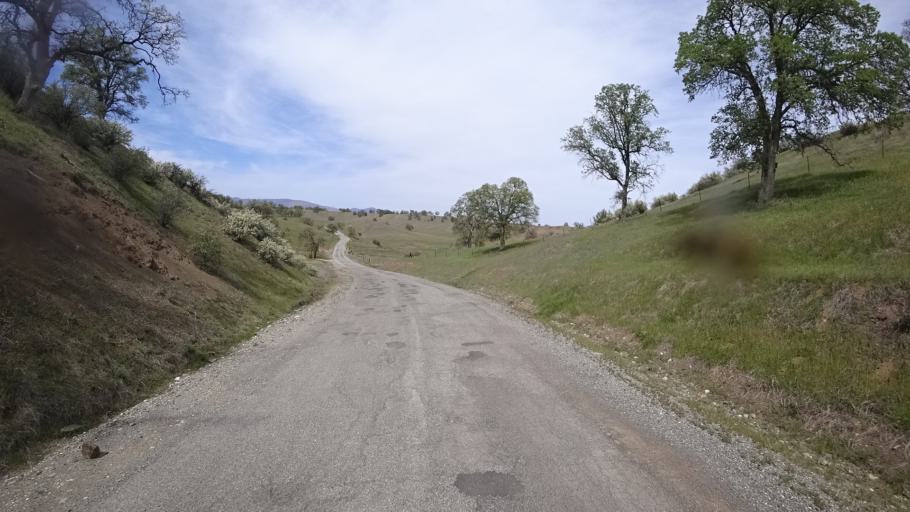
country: US
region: California
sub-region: Glenn County
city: Willows
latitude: 39.6066
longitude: -122.5587
